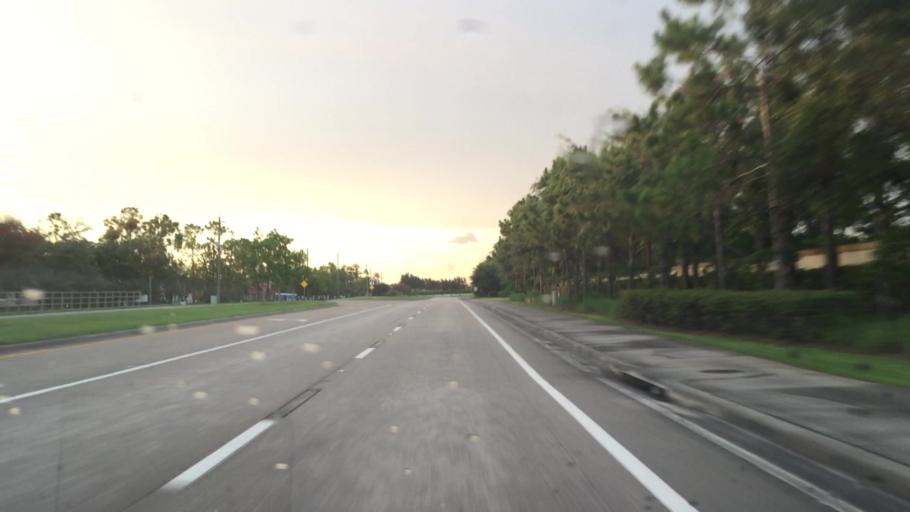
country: US
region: Florida
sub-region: Lee County
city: Gateway
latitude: 26.5618
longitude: -81.7865
